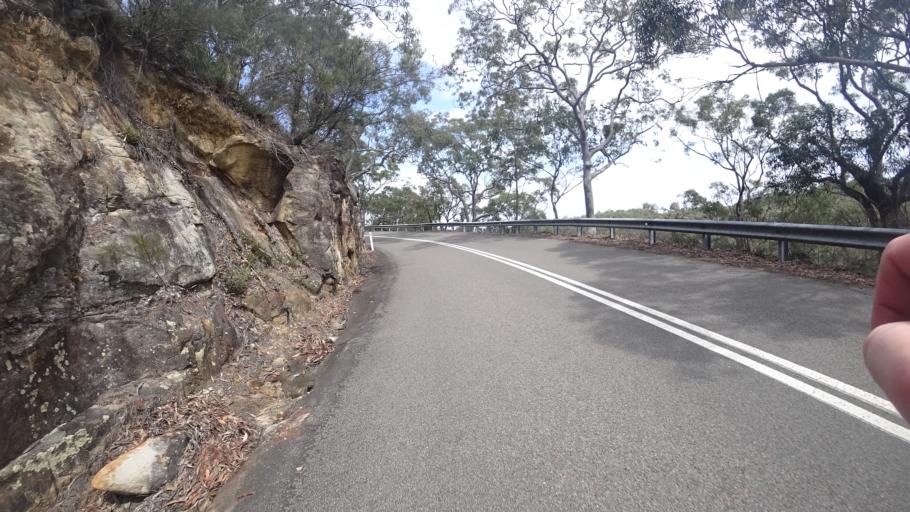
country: AU
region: New South Wales
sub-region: Hornsby Shire
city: Berowra
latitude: -33.6576
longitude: 151.1499
